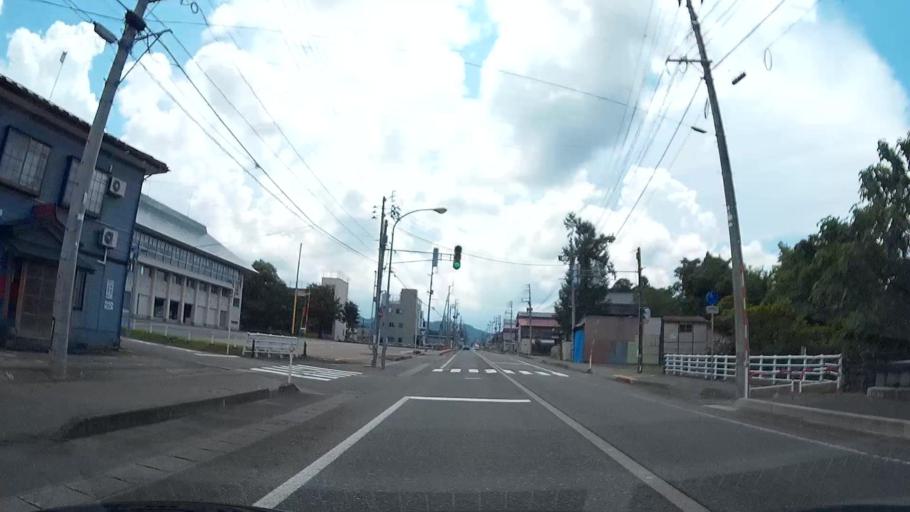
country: JP
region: Niigata
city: Tokamachi
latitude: 37.0239
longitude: 138.6609
